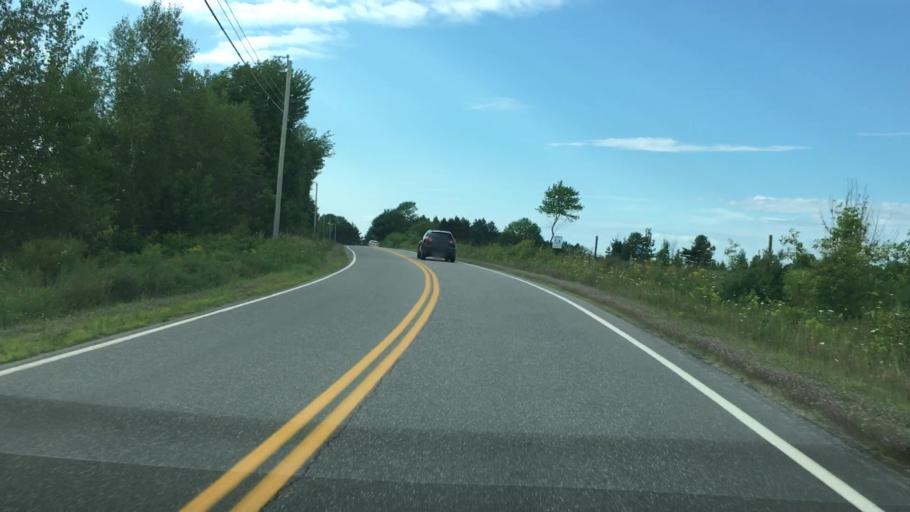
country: US
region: Maine
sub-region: Waldo County
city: Belfast
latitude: 44.3761
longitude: -69.0318
